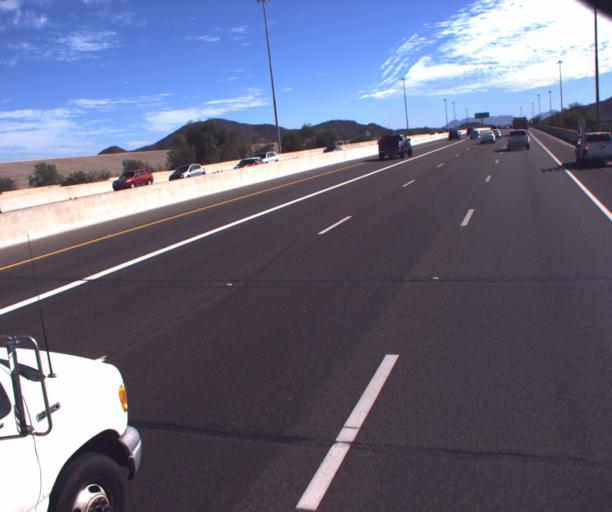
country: US
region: Arizona
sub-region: Maricopa County
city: Glendale
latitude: 33.6687
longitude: -112.0710
